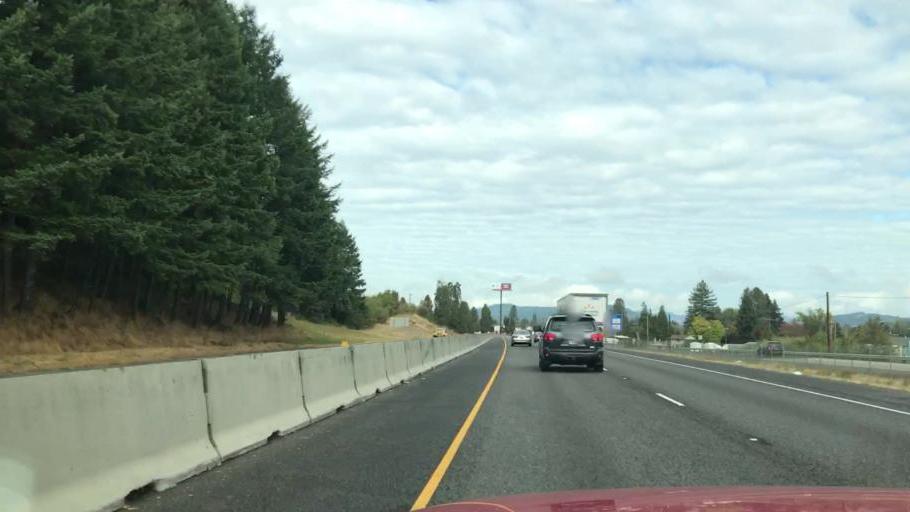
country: US
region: Oregon
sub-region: Douglas County
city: Sutherlin
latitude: 43.3741
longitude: -123.3320
